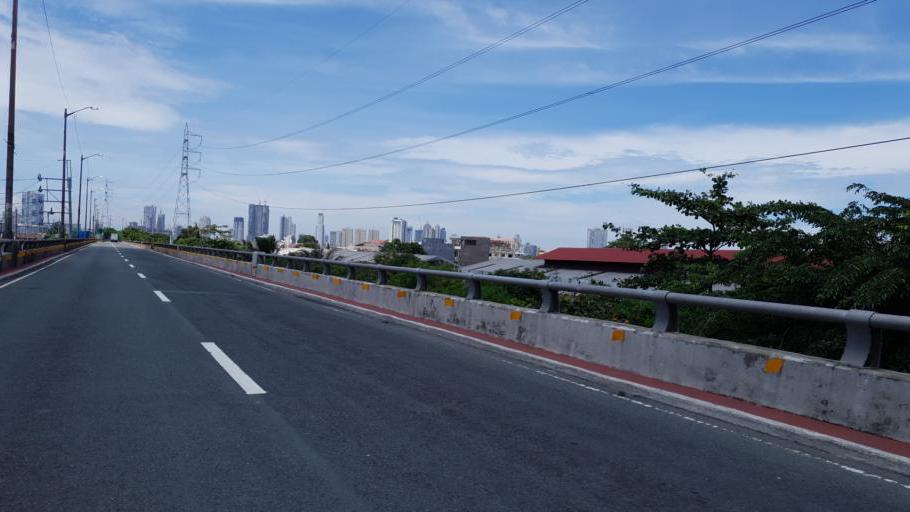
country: PH
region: Metro Manila
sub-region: San Juan
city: San Juan
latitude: 14.5906
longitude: 121.0092
